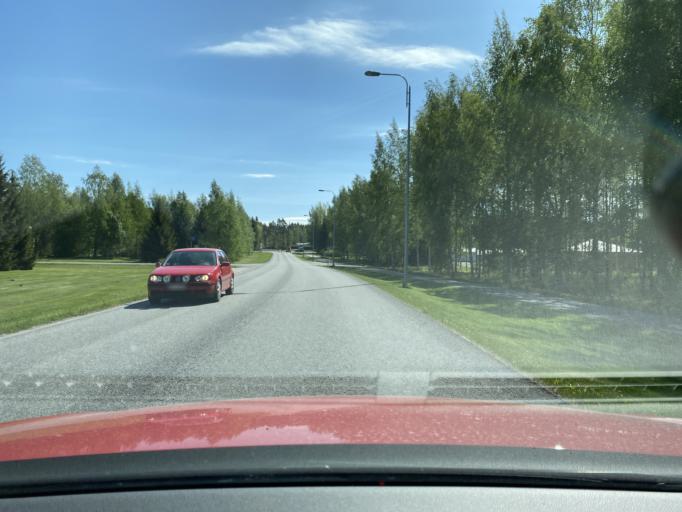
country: FI
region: Satakunta
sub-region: Rauma
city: Eura
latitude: 61.1240
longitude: 22.1557
